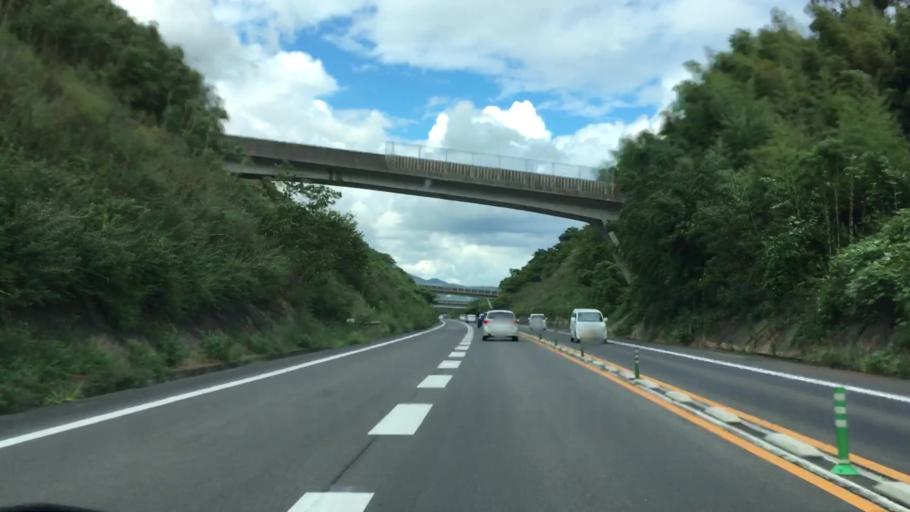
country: JP
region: Saga Prefecture
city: Karatsu
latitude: 33.4209
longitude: 130.0308
